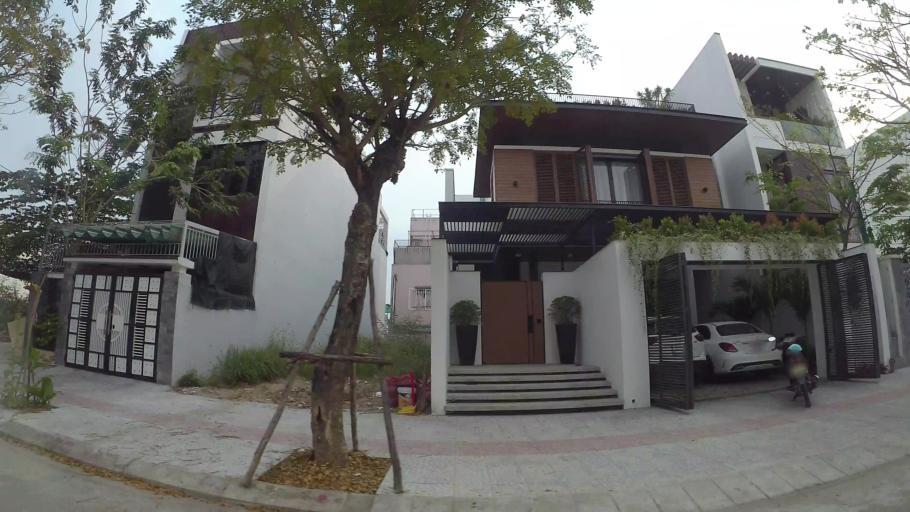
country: VN
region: Da Nang
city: Cam Le
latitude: 16.0219
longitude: 108.2287
